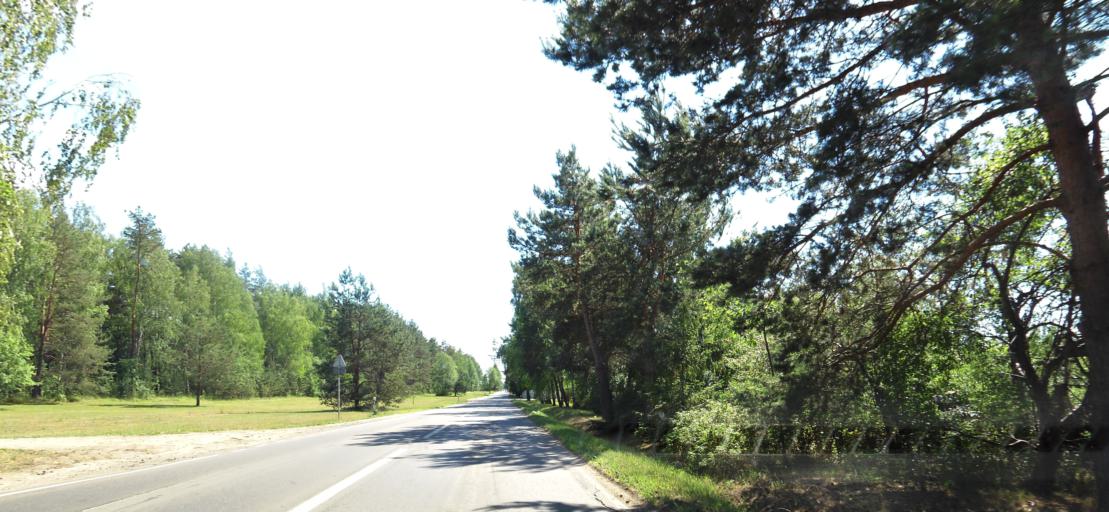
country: LT
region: Vilnius County
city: Rasos
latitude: 54.7902
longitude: 25.3514
